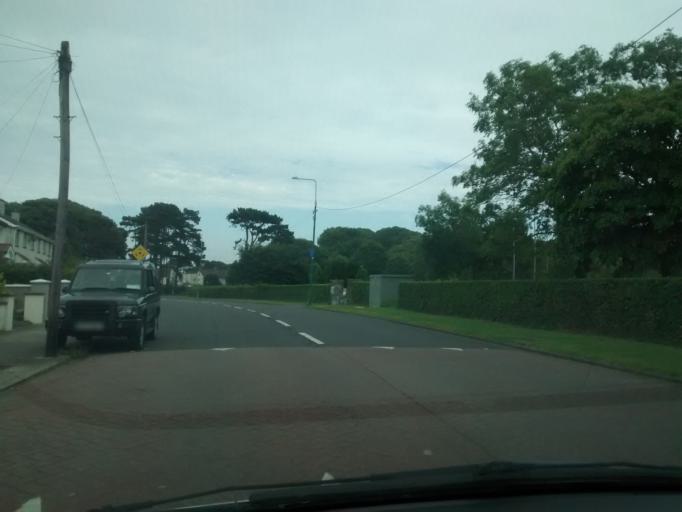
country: IE
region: Leinster
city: Dollymount
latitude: 53.3751
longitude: -6.1819
